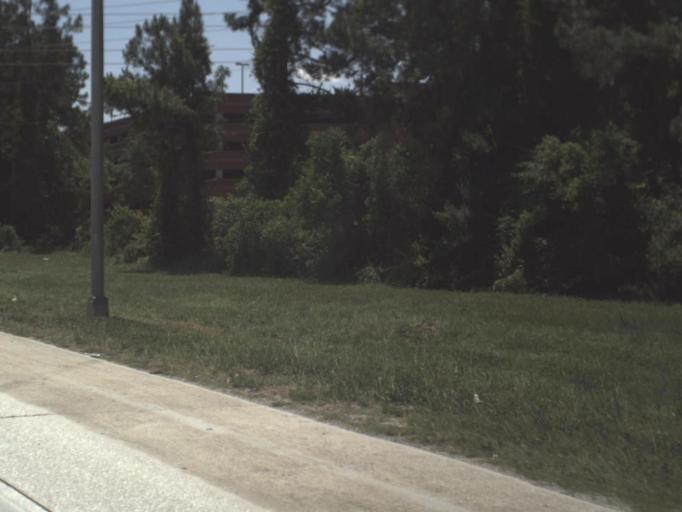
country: US
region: Florida
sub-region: Duval County
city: Jacksonville
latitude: 30.2357
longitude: -81.5812
